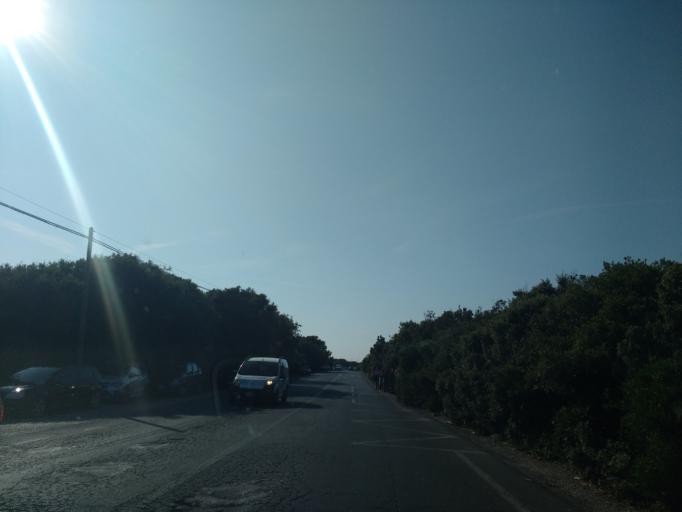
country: IT
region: Latium
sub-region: Citta metropolitana di Roma Capitale
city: Torvaianica
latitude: 41.6764
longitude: 12.3902
